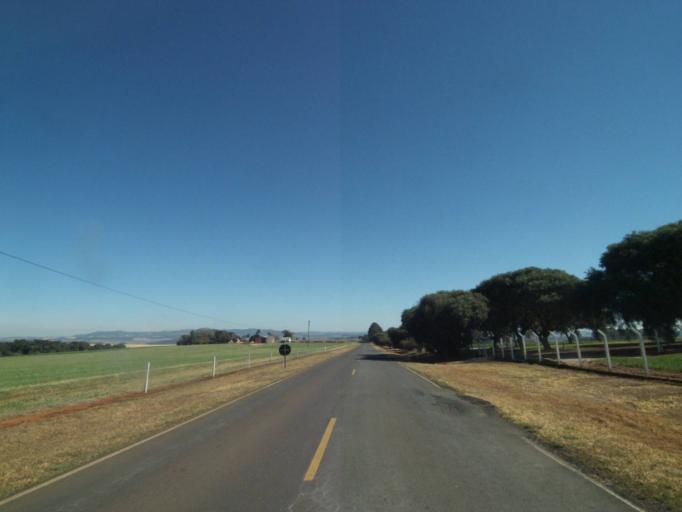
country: BR
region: Parana
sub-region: Tibagi
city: Tibagi
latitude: -24.5248
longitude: -50.3706
